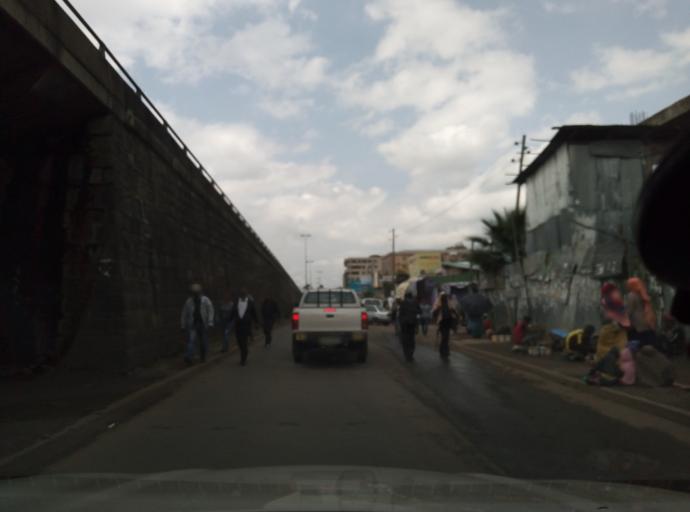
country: ET
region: Adis Abeba
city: Addis Ababa
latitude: 9.0098
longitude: 38.7203
